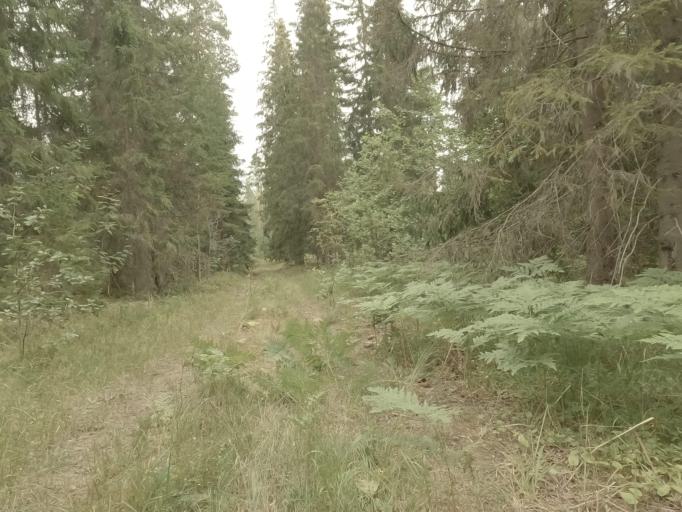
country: RU
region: Leningrad
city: Kamennogorsk
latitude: 61.0481
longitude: 29.1847
